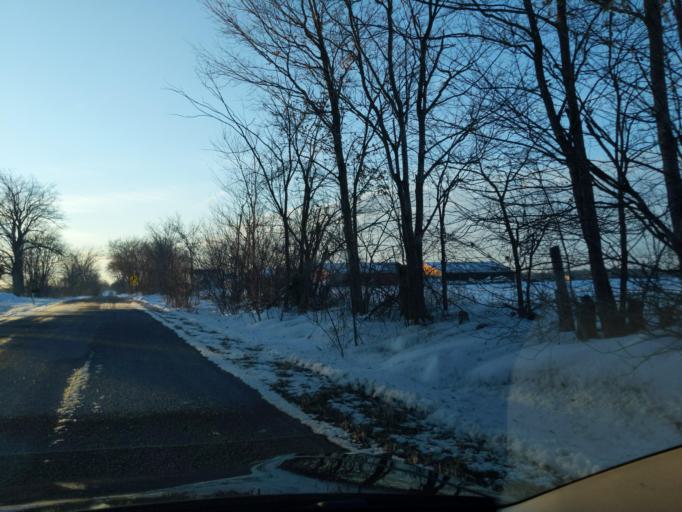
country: US
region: Michigan
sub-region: Ingham County
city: Webberville
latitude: 42.5699
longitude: -84.1993
